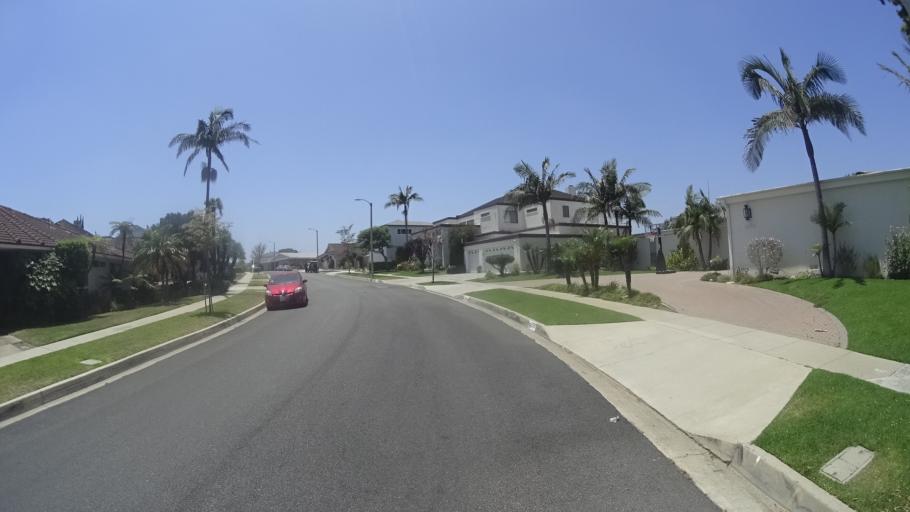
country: US
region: California
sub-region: Los Angeles County
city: View Park-Windsor Hills
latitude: 34.0033
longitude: -118.3505
